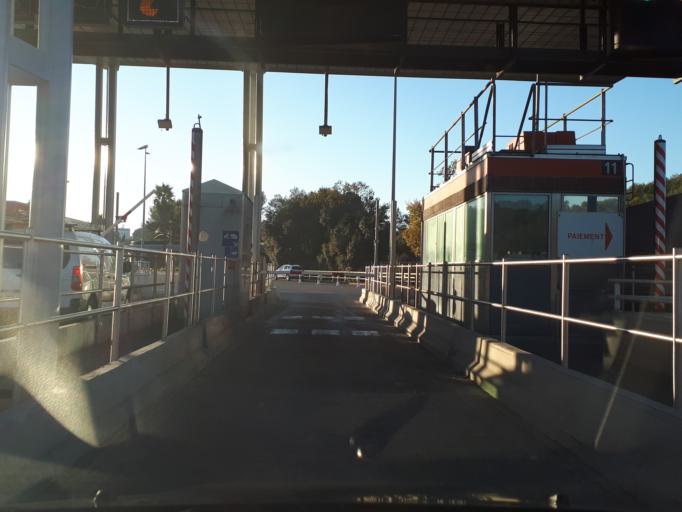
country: FR
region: Provence-Alpes-Cote d'Azur
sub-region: Departement des Alpes-Maritimes
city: Vallauris
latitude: 43.6051
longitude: 7.0665
